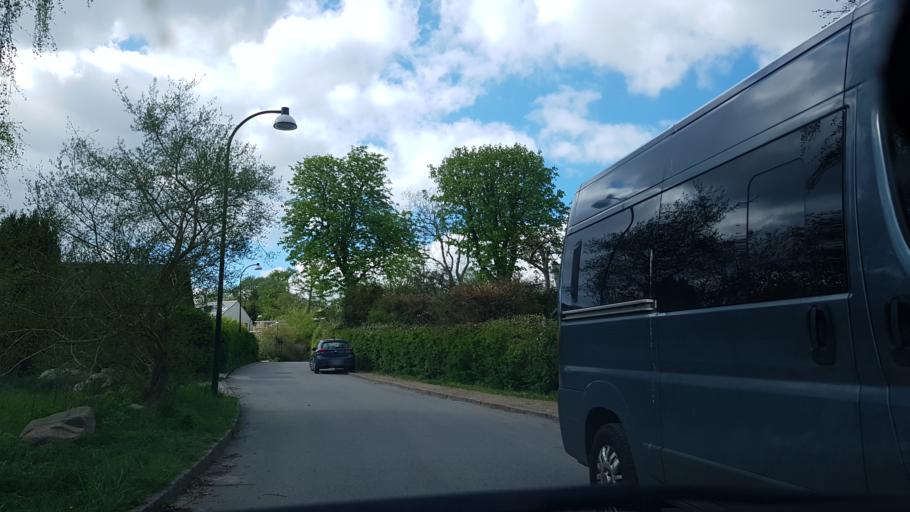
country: DK
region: Capital Region
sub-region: Rudersdal Kommune
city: Holte
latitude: 55.8162
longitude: 12.4937
